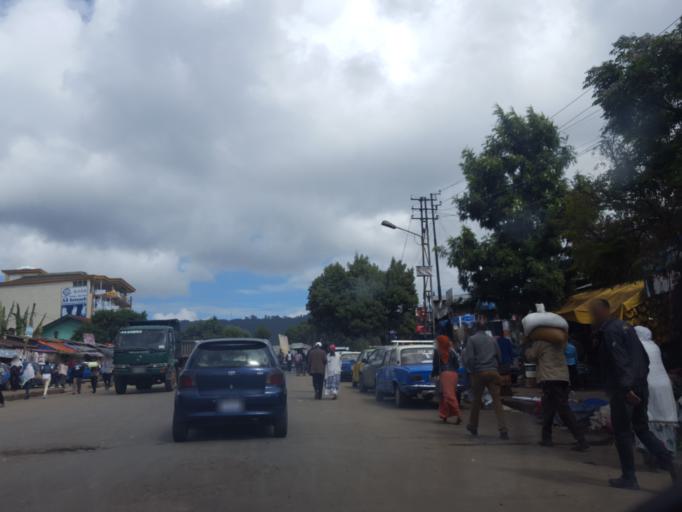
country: ET
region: Adis Abeba
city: Addis Ababa
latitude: 9.0615
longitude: 38.7615
